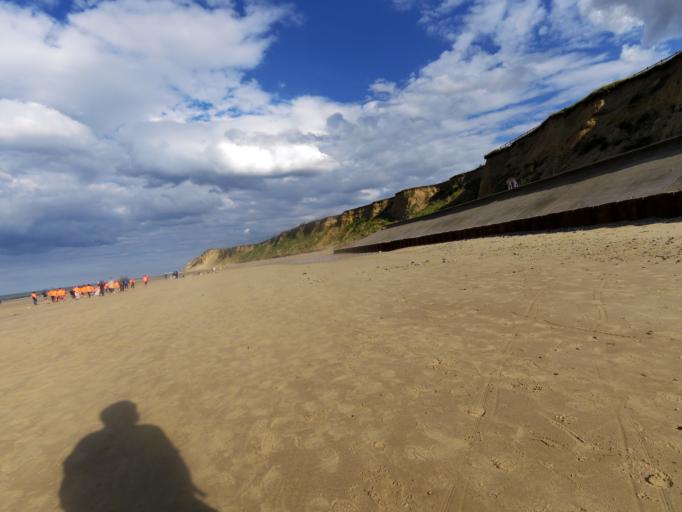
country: GB
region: England
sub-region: Norfolk
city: Sheringham
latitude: 52.9415
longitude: 1.2521
